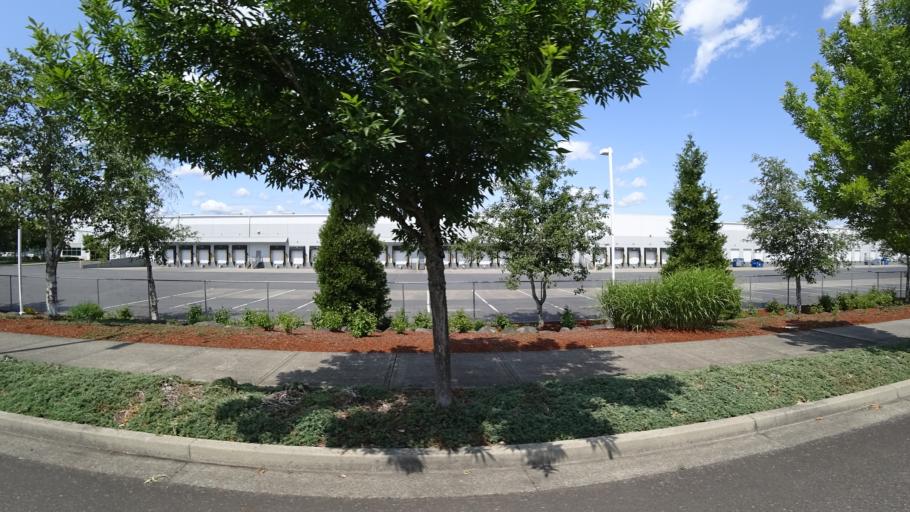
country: US
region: Washington
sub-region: Clark County
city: Lake Shore
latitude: 45.6299
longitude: -122.7554
